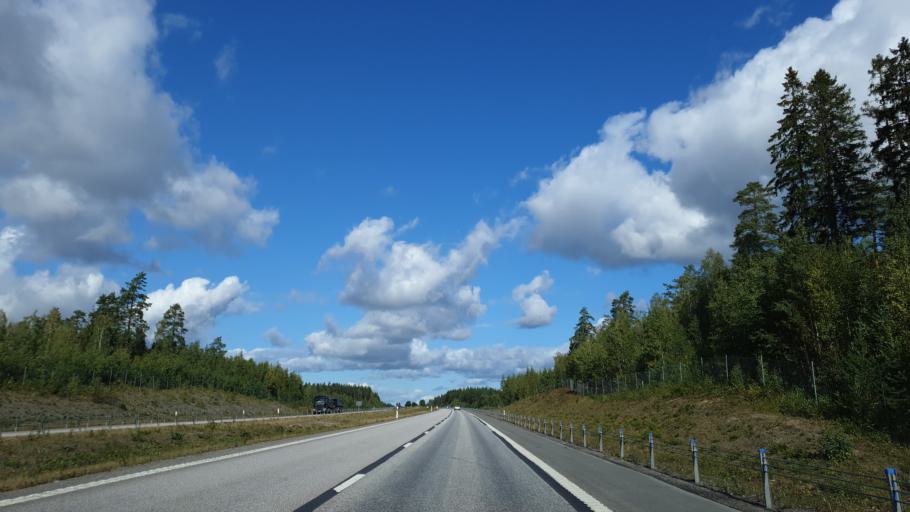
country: SE
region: Uppsala
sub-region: Tierps Kommun
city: Tierp
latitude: 60.2361
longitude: 17.5019
